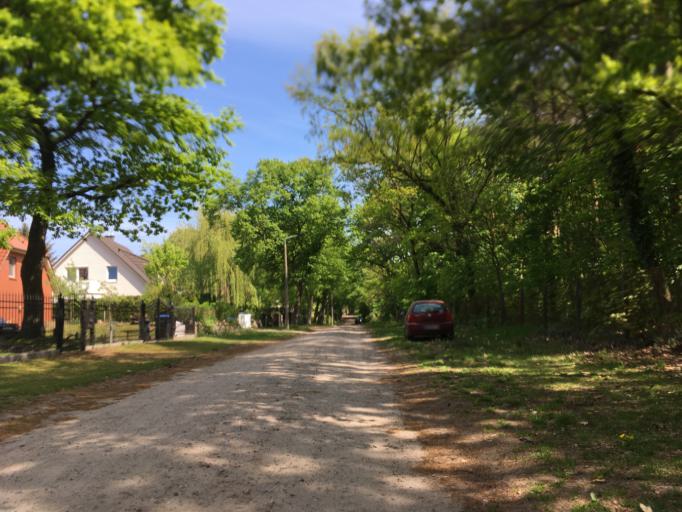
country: DE
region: Berlin
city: Blankenfelde
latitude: 52.6449
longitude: 13.3883
